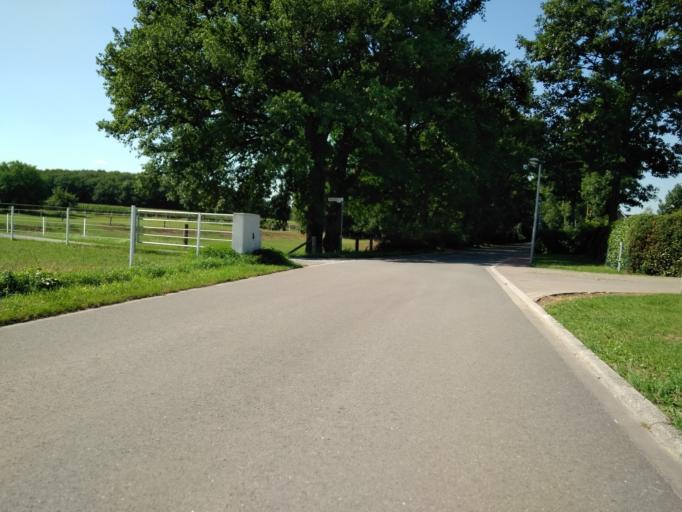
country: DE
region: North Rhine-Westphalia
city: Dorsten
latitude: 51.6713
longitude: 6.9314
